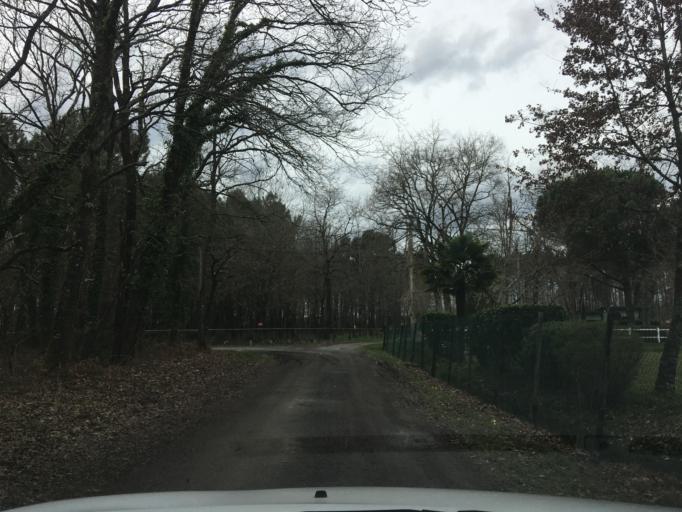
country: FR
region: Aquitaine
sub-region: Departement de la Gironde
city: Saint-Sauveur
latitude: 45.2229
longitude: -0.8705
